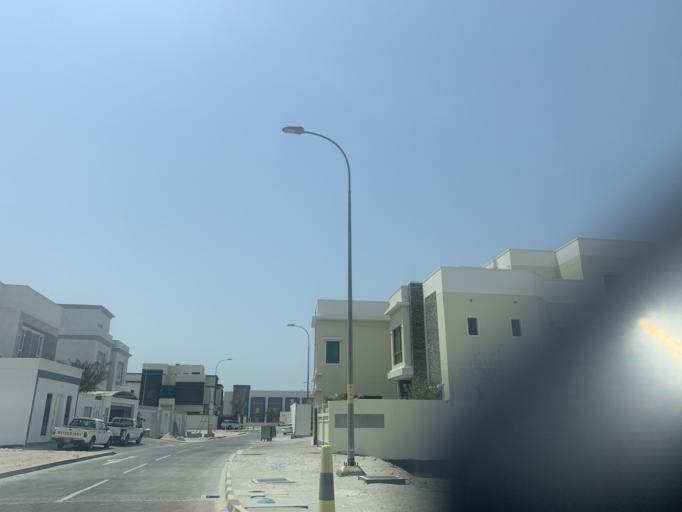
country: BH
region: Muharraq
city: Al Muharraq
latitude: 26.2980
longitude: 50.6389
